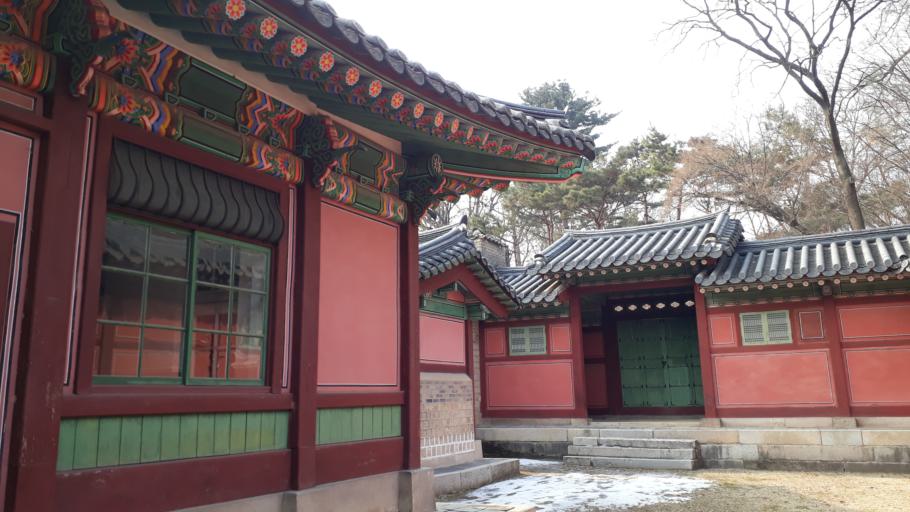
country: KR
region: Seoul
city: Seoul
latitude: 37.5772
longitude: 126.9906
